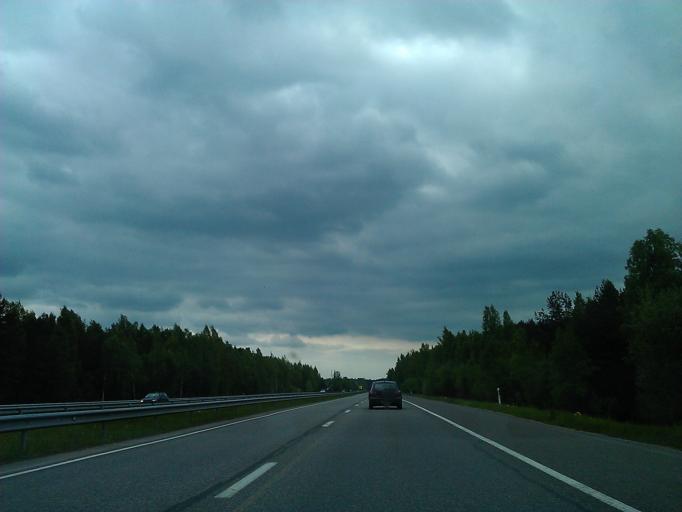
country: LV
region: Marupe
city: Marupe
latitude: 56.8623
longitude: 24.0648
